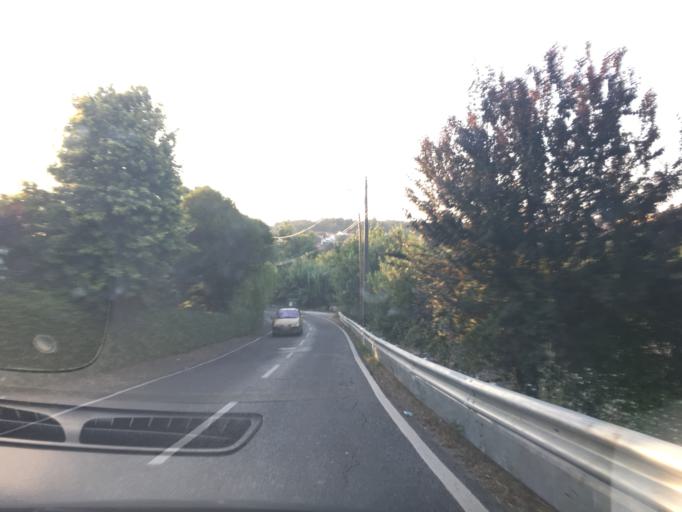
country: PT
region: Lisbon
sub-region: Sintra
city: Sintra
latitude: 38.8113
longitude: -9.3894
